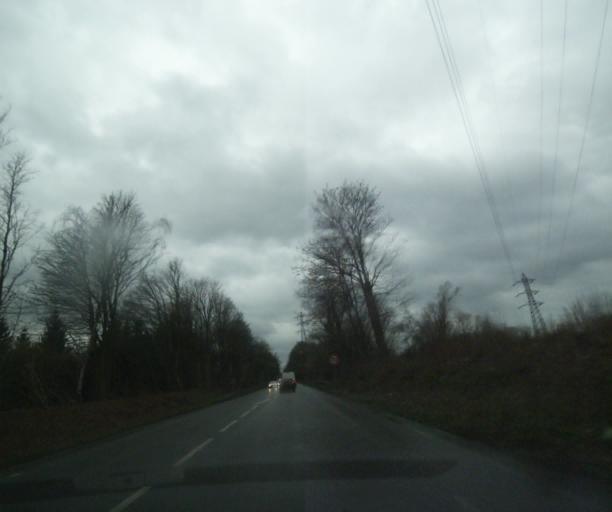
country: FR
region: Nord-Pas-de-Calais
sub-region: Departement du Nord
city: Saint-Saulve
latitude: 50.3840
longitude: 3.5491
